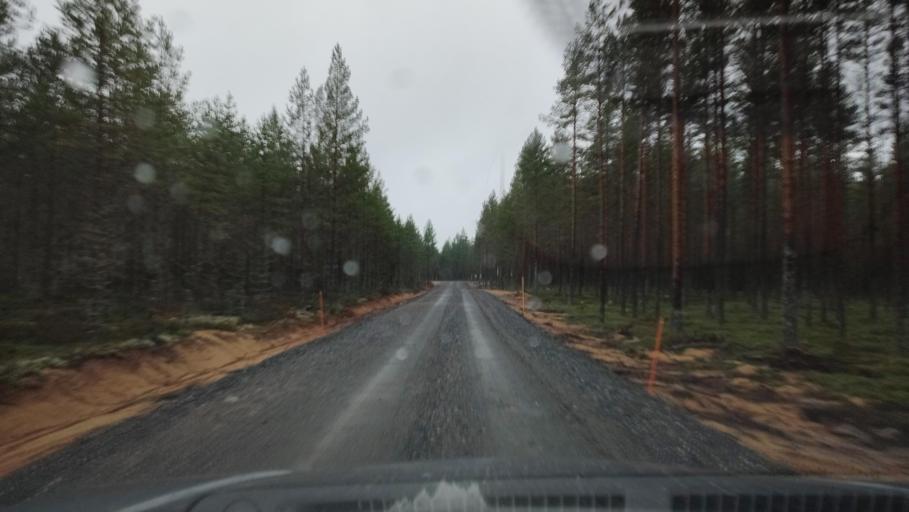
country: FI
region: Southern Ostrobothnia
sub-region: Suupohja
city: Karijoki
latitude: 62.1489
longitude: 21.6249
